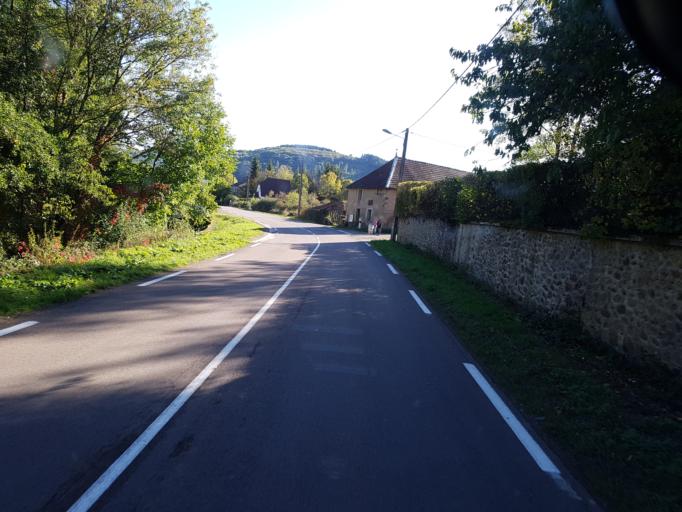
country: FR
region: Bourgogne
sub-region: Departement de Saone-et-Loire
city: Autun
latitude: 47.1029
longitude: 4.2308
